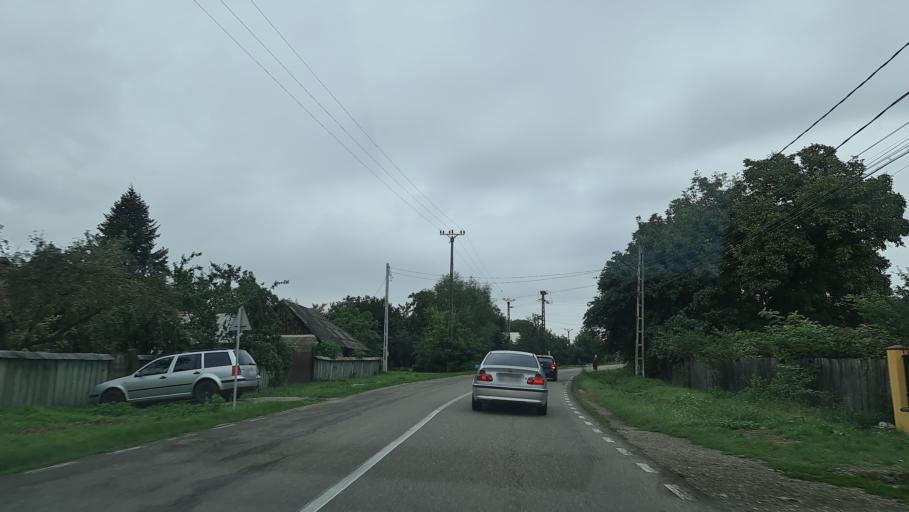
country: RO
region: Neamt
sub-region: Comuna Stefan cel Mare
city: Stefan cel Mare
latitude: 46.9654
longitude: 26.4701
